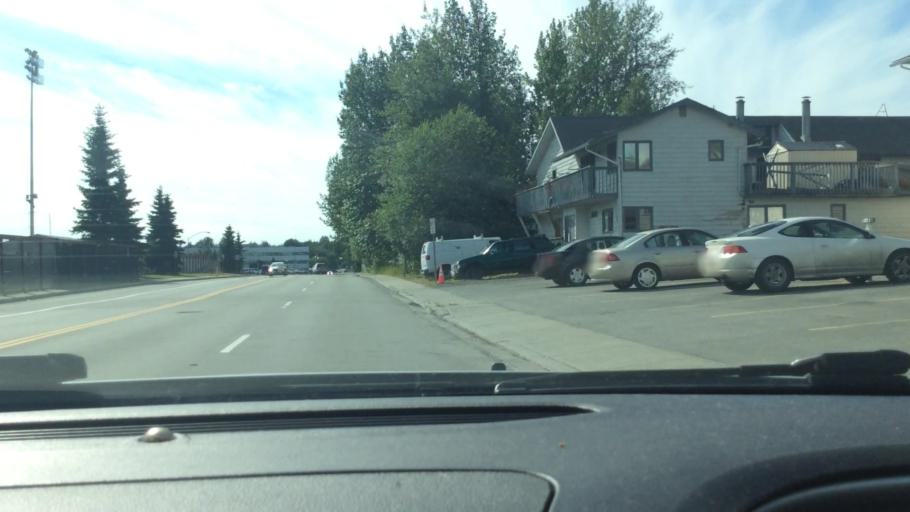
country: US
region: Alaska
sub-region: Anchorage Municipality
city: Anchorage
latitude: 61.2061
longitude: -149.8759
